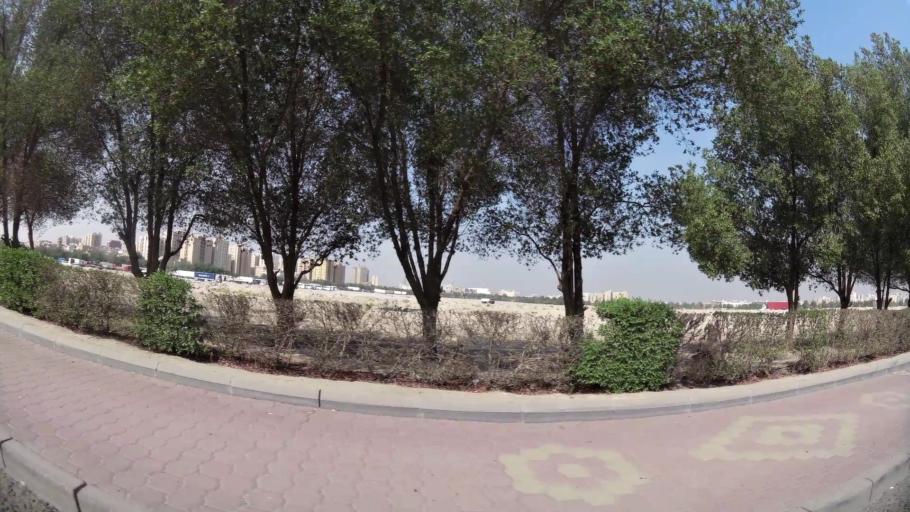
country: KW
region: Al Farwaniyah
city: Al Farwaniyah
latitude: 29.2546
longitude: 47.9493
